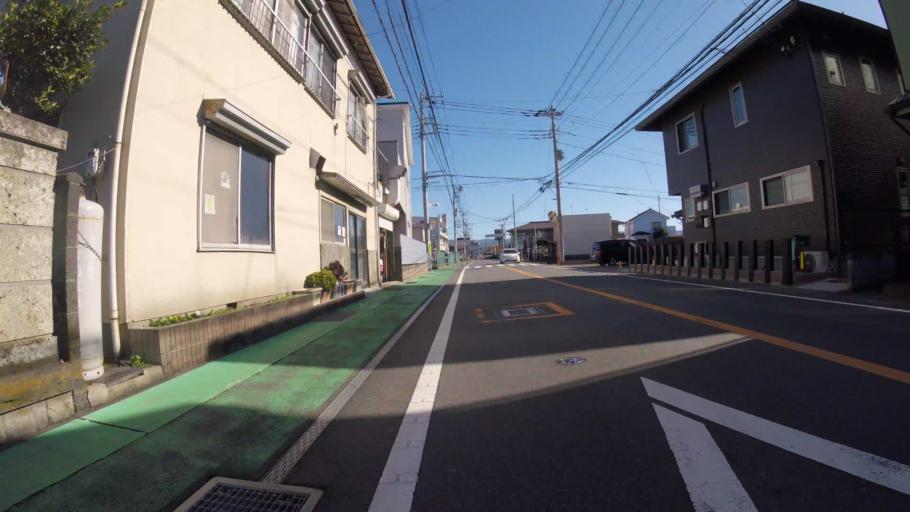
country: JP
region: Shizuoka
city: Mishima
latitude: 35.1201
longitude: 138.8936
